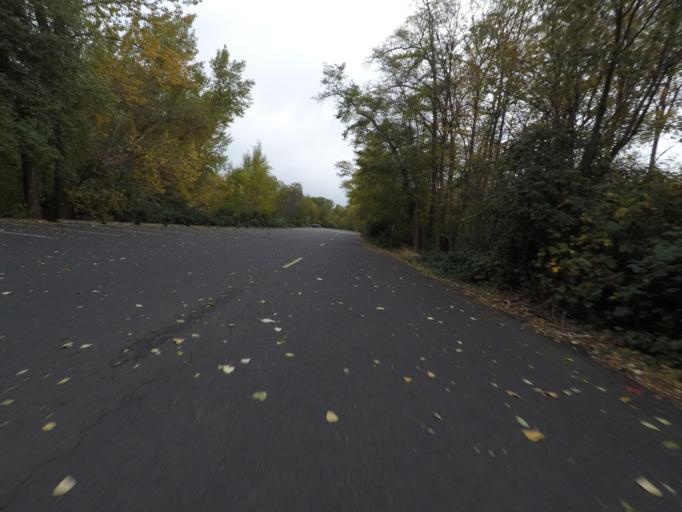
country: US
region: Washington
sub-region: Walla Walla County
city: Walla Walla East
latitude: 46.0822
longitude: -118.2545
